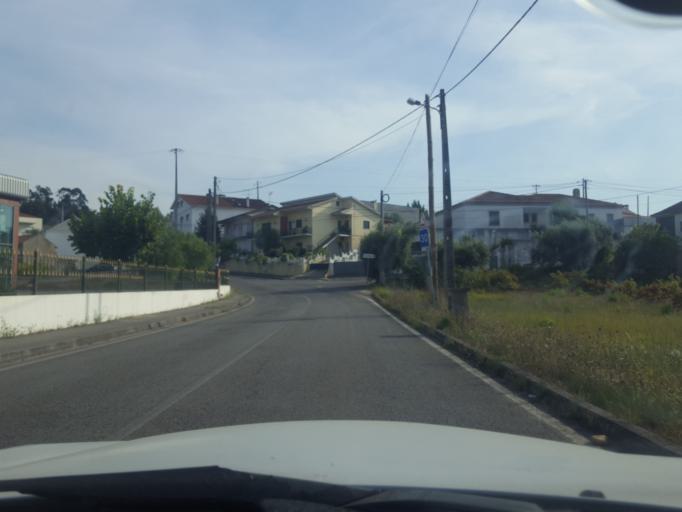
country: PT
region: Leiria
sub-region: Leiria
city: Leiria
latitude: 39.7178
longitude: -8.7834
